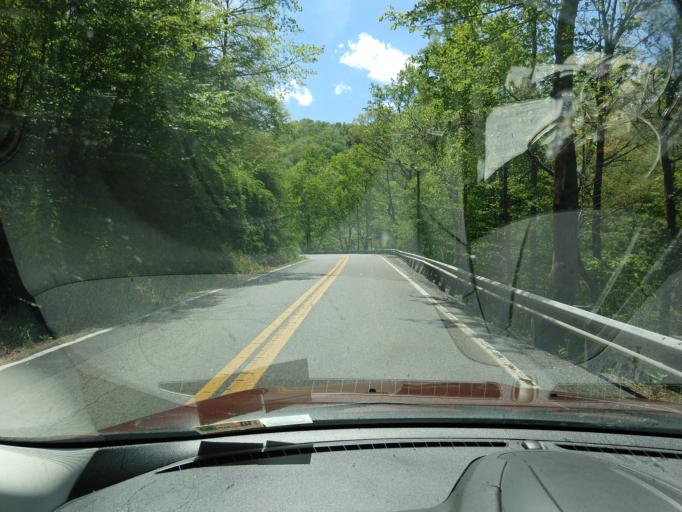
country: US
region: West Virginia
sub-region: McDowell County
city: Welch
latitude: 37.3149
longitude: -81.6964
